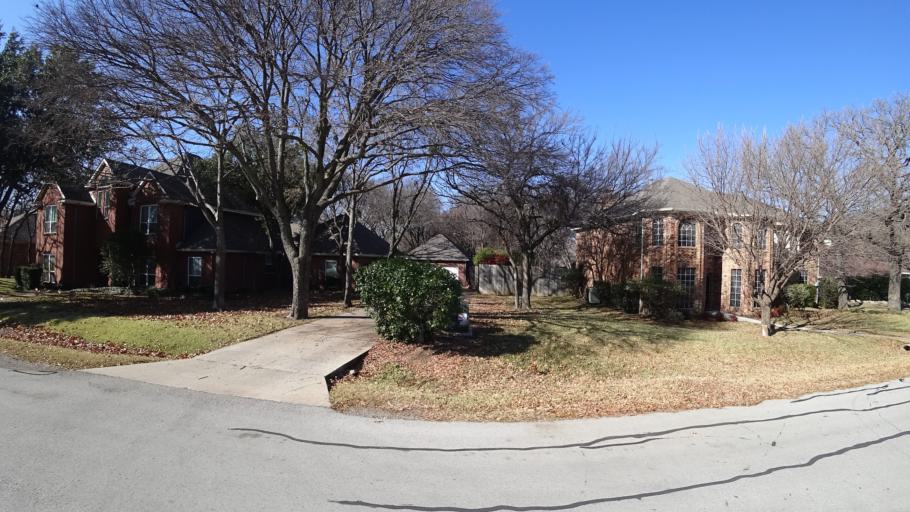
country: US
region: Texas
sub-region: Denton County
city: Lewisville
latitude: 33.0148
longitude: -97.0214
